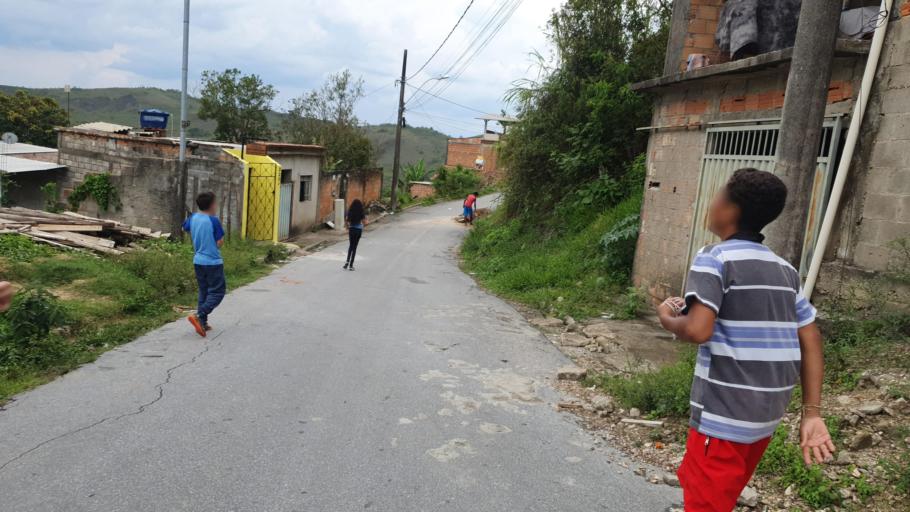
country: BR
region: Minas Gerais
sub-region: Sao Joao Del Rei
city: Sao Joao del Rei
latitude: -21.1271
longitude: -44.2657
